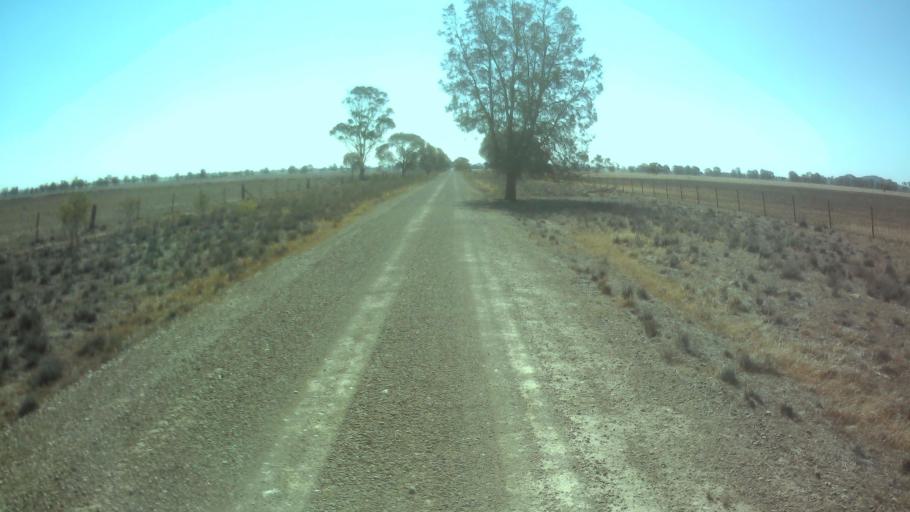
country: AU
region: New South Wales
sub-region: Weddin
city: Grenfell
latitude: -33.7597
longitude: 147.7071
